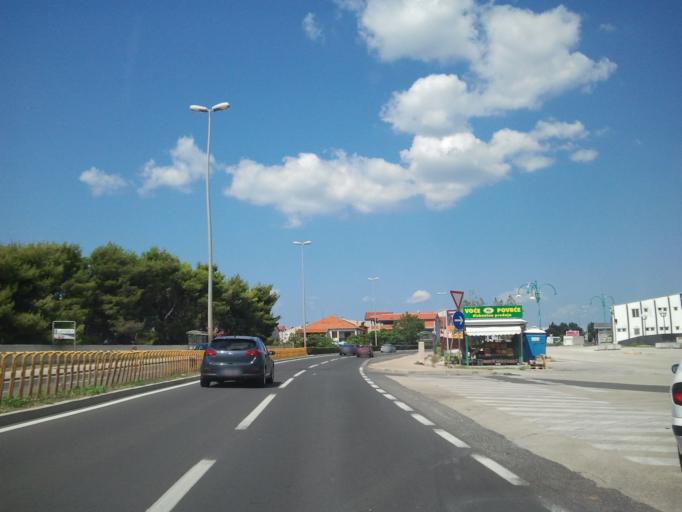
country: HR
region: Zadarska
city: Zadar
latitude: 44.1113
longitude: 15.2561
